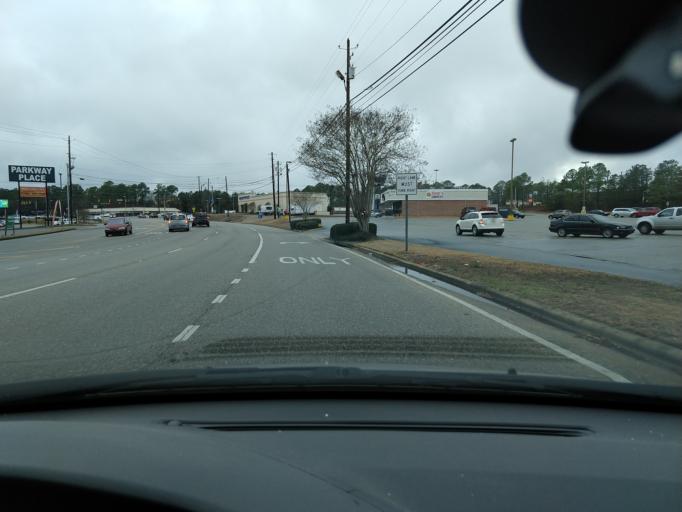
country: US
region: Alabama
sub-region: Houston County
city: Dothan
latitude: 31.2585
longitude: -85.4317
